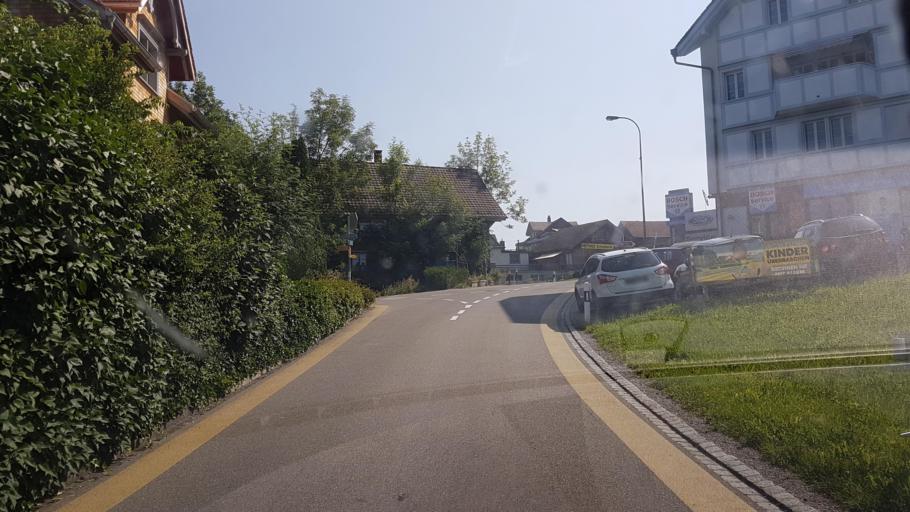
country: CH
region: Saint Gallen
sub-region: Wahlkreis Toggenburg
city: Mogelsberg
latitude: 47.3628
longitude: 9.1336
